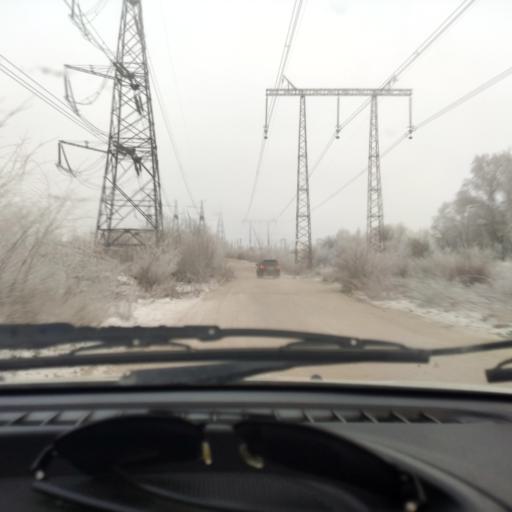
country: RU
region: Samara
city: Zhigulevsk
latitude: 53.4784
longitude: 49.5054
